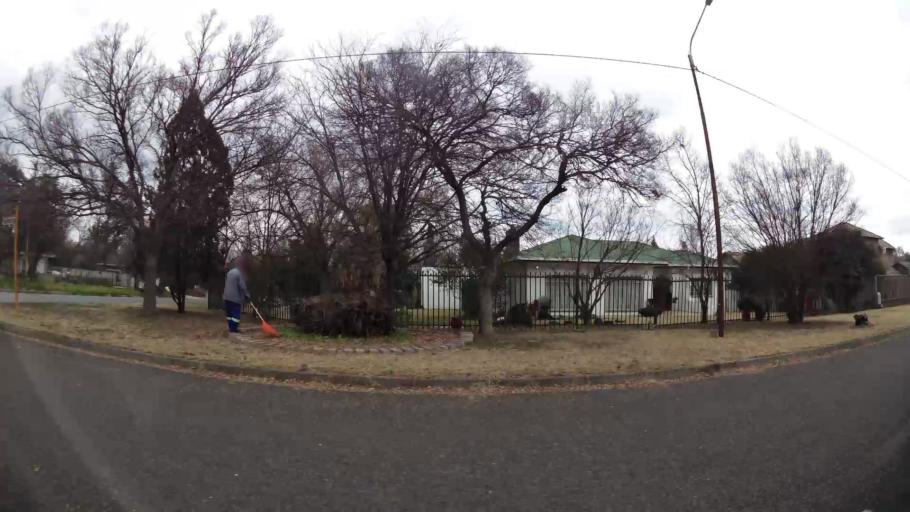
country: ZA
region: Orange Free State
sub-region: Fezile Dabi District Municipality
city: Kroonstad
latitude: -27.6804
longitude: 27.2444
